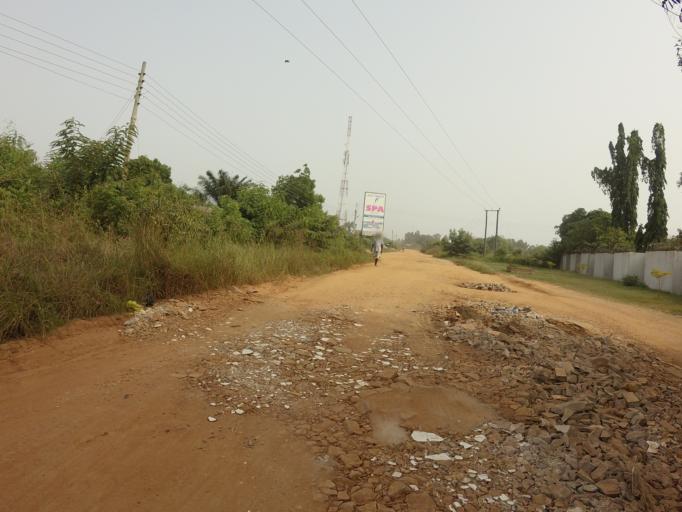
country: GH
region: Volta
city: Anloga
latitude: 5.9913
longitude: 0.5943
